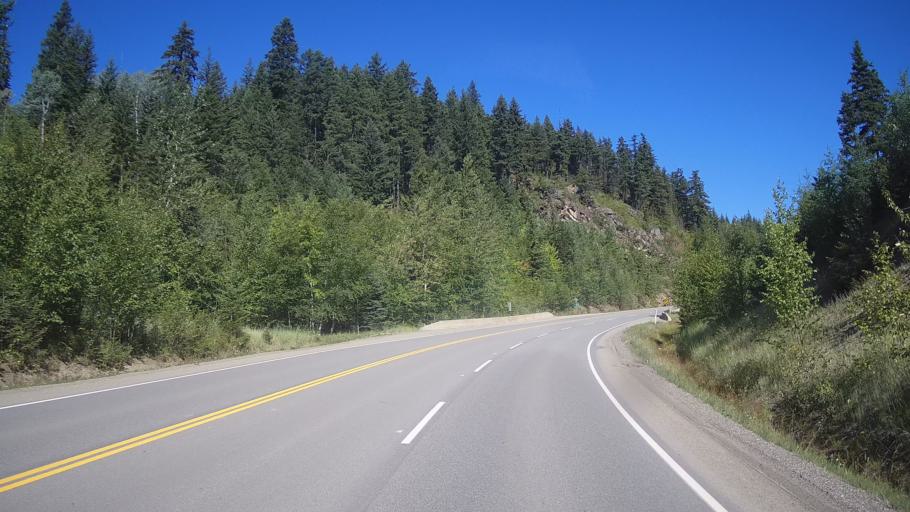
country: CA
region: British Columbia
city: Kamloops
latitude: 51.4625
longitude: -120.2470
